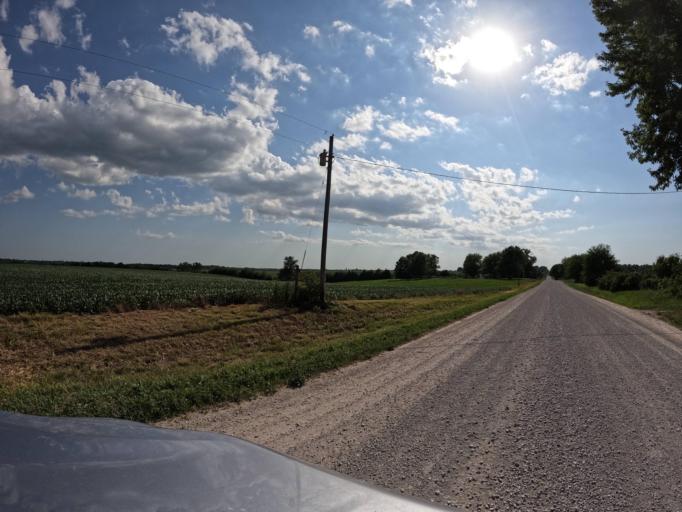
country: US
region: Iowa
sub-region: Appanoose County
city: Centerville
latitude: 40.7178
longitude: -93.0182
